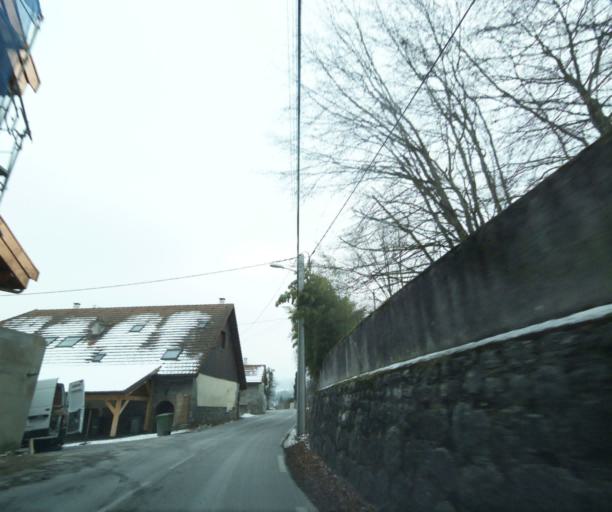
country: FR
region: Rhone-Alpes
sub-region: Departement de la Haute-Savoie
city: Reignier-Esery
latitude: 46.1335
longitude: 6.2599
